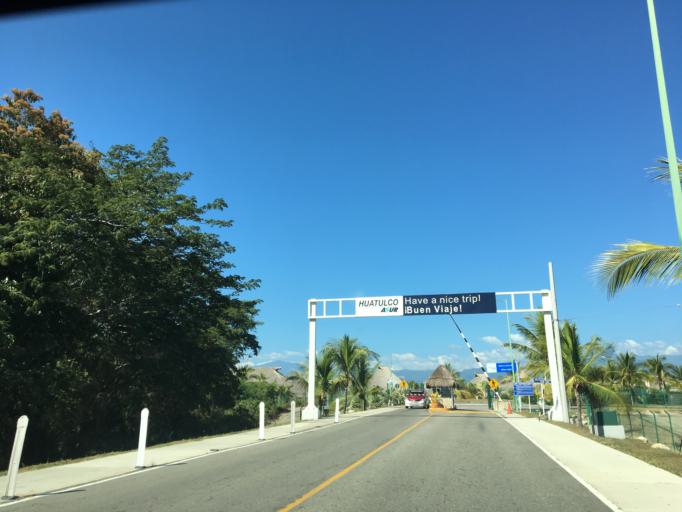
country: MX
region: Oaxaca
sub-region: Santa Maria Huatulco
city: Cuapinolito (Azulillo)
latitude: 15.7696
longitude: -96.2584
